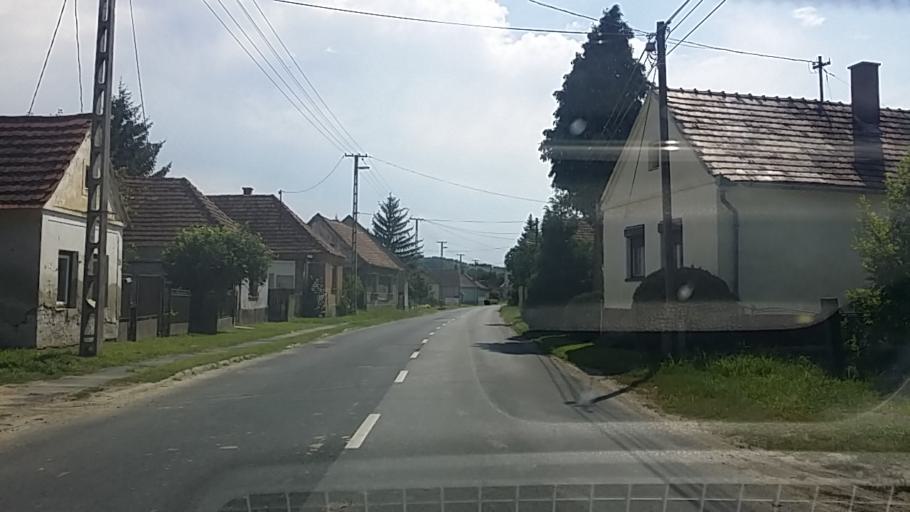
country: HR
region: Medimurska
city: Podturen
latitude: 46.5165
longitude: 16.5786
